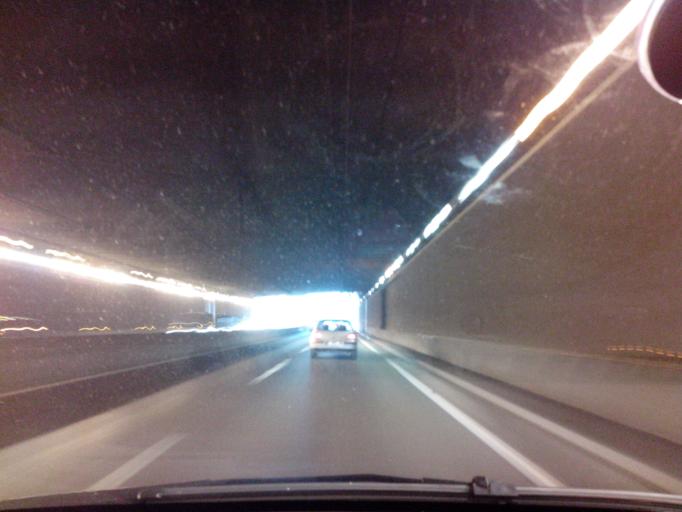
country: FR
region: Ile-de-France
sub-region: Departement du Val-de-Marne
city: Fresnes
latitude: 48.7581
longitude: 2.3266
